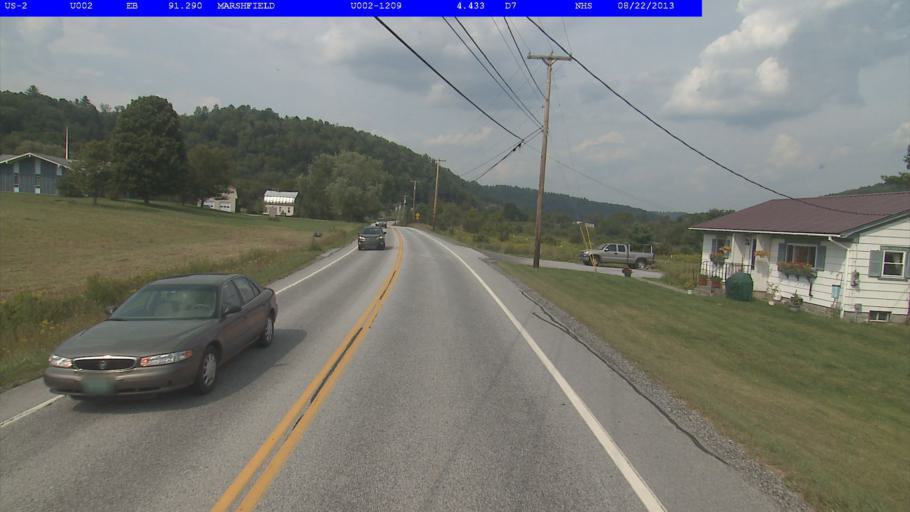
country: US
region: Vermont
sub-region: Caledonia County
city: Hardwick
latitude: 44.3285
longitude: -72.3764
